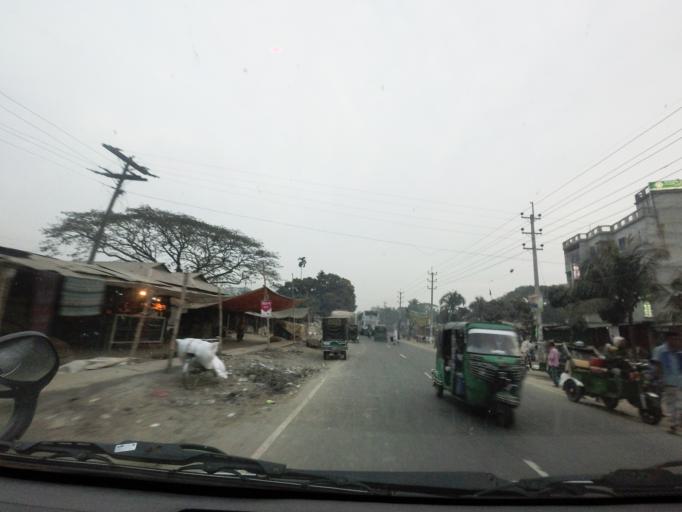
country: BD
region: Dhaka
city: Bajitpur
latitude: 24.2091
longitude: 90.8557
